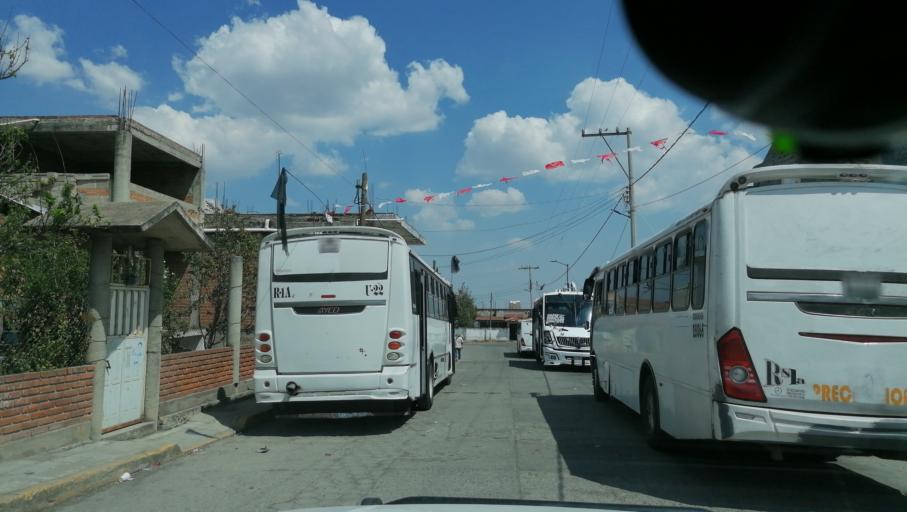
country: MX
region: Puebla
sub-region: San Nicolas de los Ranchos
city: San Pedro Yancuitlalpan
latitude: 19.1036
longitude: -98.4847
